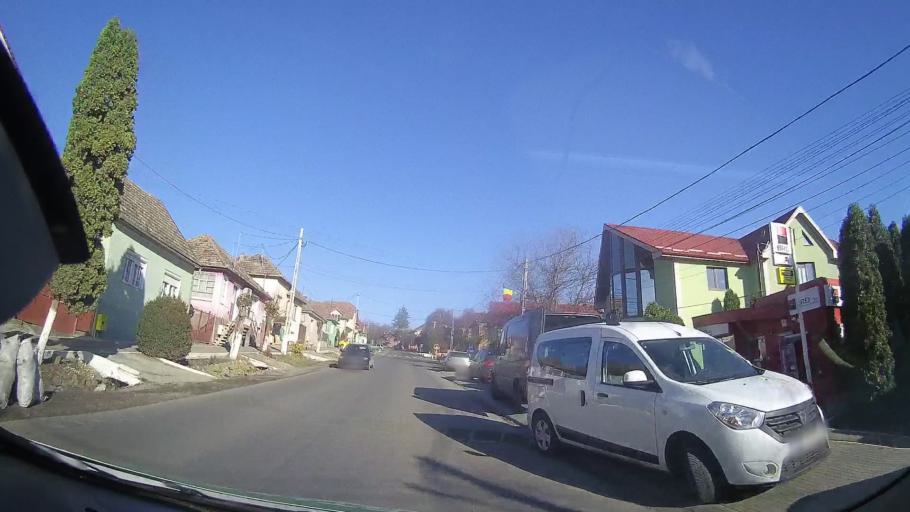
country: RO
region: Mures
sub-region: Comuna Sarmasu
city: Sarmasu
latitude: 46.7542
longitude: 24.1627
